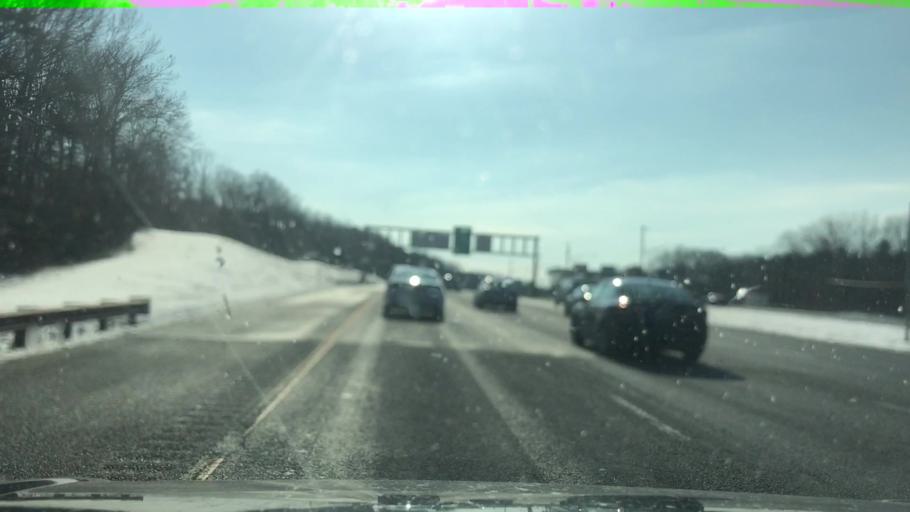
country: US
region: New Jersey
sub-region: Monmouth County
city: Shark River Hills
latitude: 40.1759
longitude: -74.1006
